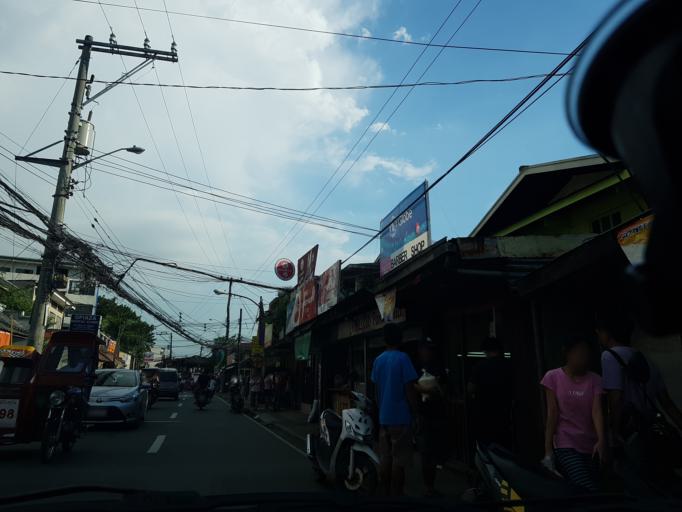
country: PH
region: Metro Manila
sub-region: Marikina
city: Calumpang
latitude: 14.6160
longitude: 121.0815
